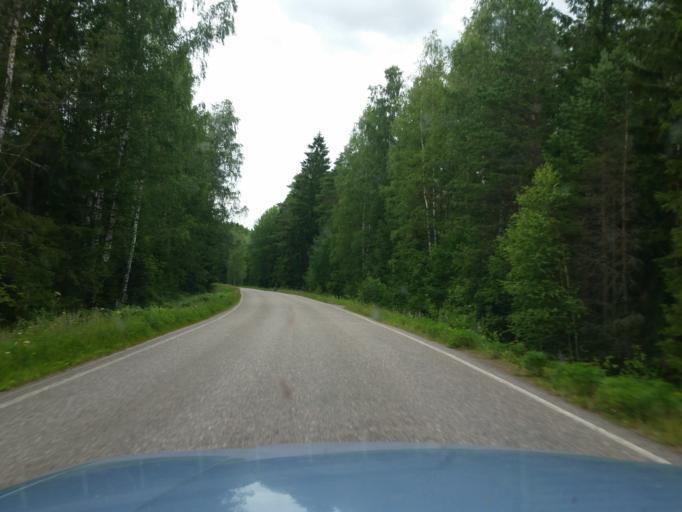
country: FI
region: Uusimaa
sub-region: Helsinki
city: Sammatti
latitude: 60.4222
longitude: 23.8254
